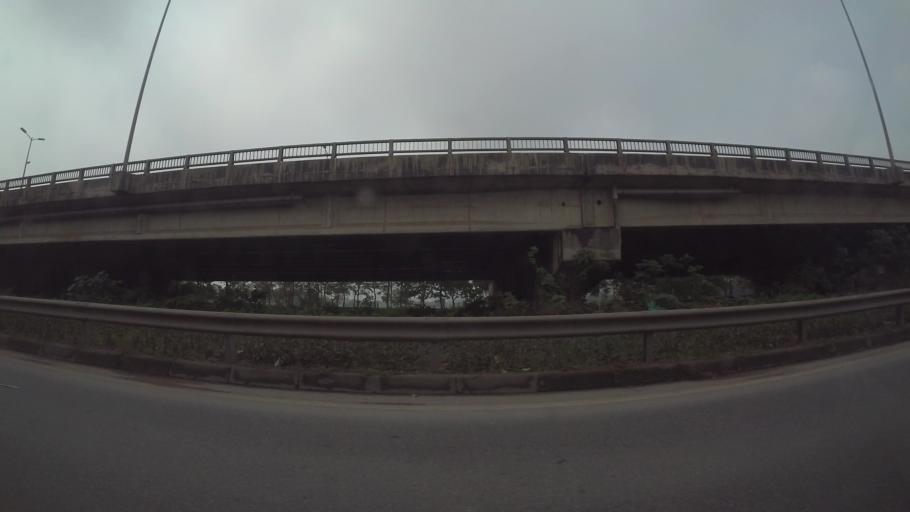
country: VN
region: Ha Noi
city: Van Dien
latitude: 20.9658
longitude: 105.8522
